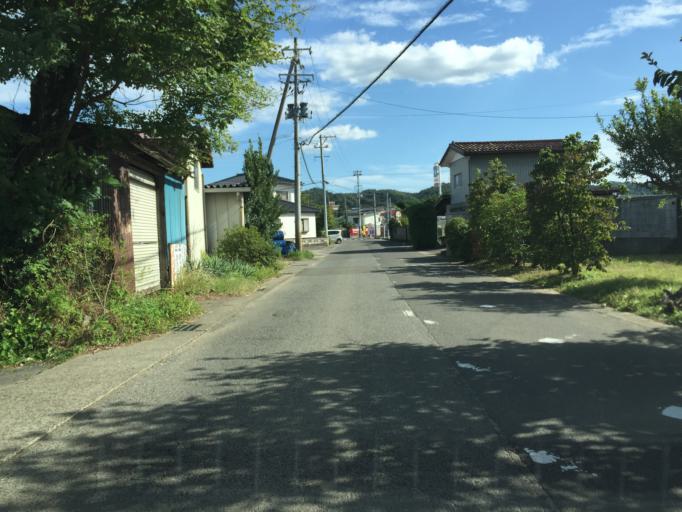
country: JP
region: Fukushima
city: Yanagawamachi-saiwaicho
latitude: 37.8374
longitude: 140.5959
